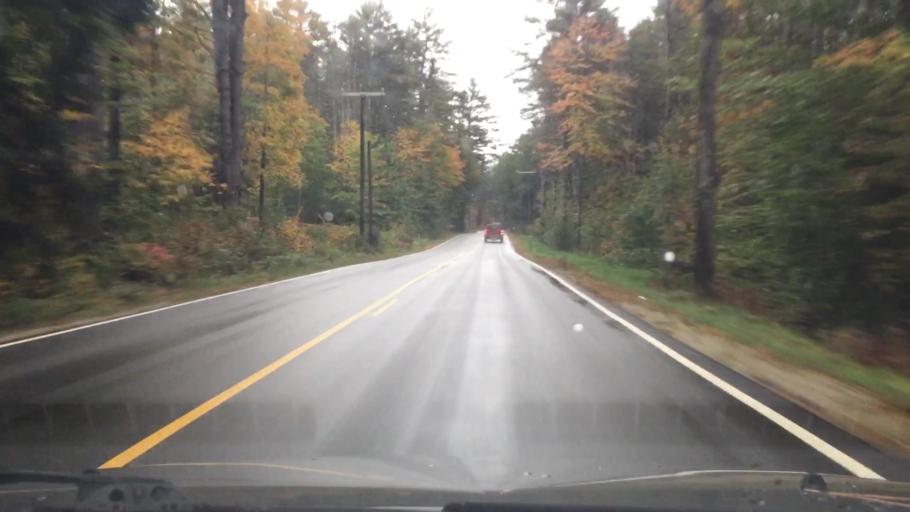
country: US
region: New Hampshire
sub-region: Cheshire County
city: Swanzey
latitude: 42.8390
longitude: -72.2779
